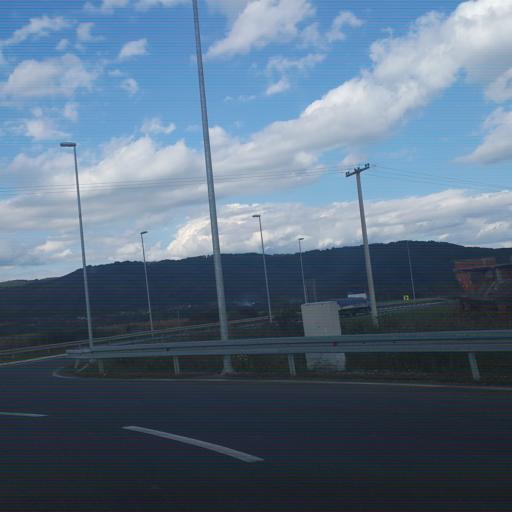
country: RS
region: Central Serbia
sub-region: Rasinski Okrug
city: Krusevac
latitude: 43.5863
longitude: 21.2495
